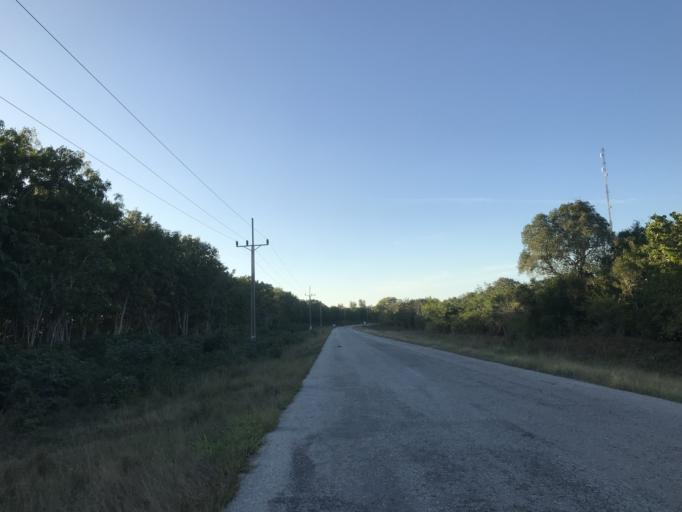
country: CU
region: Cienfuegos
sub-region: Municipio de Aguada de Pasajeros
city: Aguada de Pasajeros
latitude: 22.0685
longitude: -81.0501
